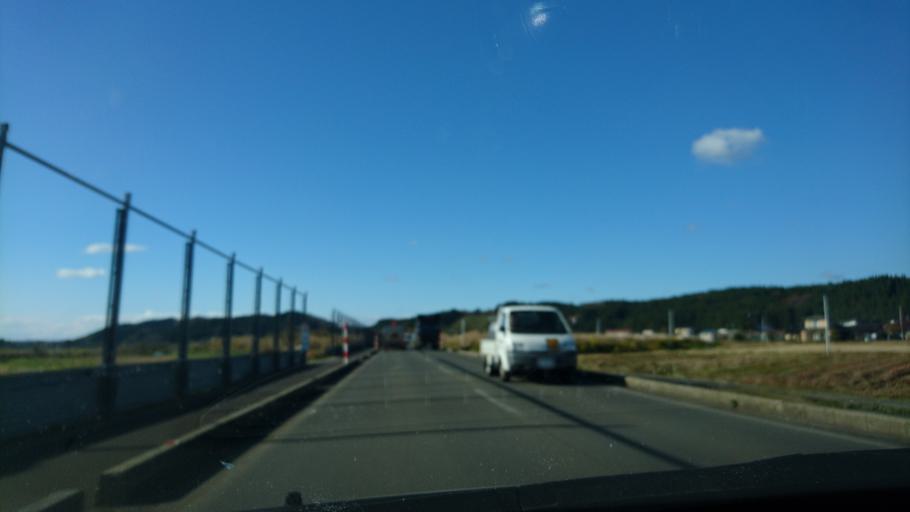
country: JP
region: Akita
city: Akita
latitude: 39.3462
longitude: 140.1158
